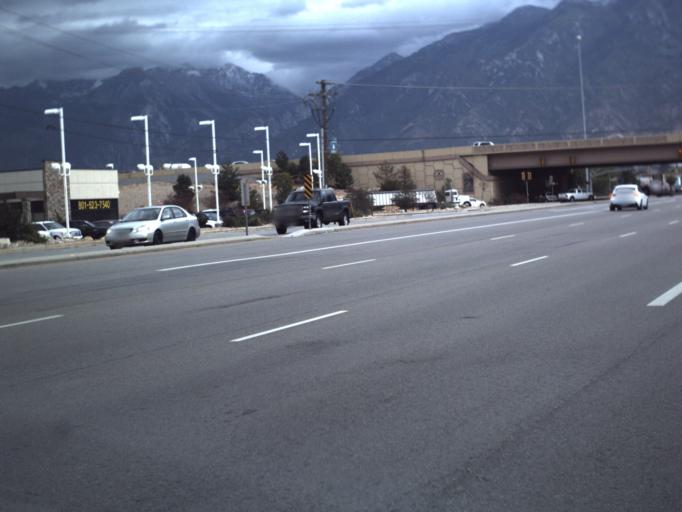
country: US
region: Utah
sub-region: Salt Lake County
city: Draper
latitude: 40.5266
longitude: -111.8938
